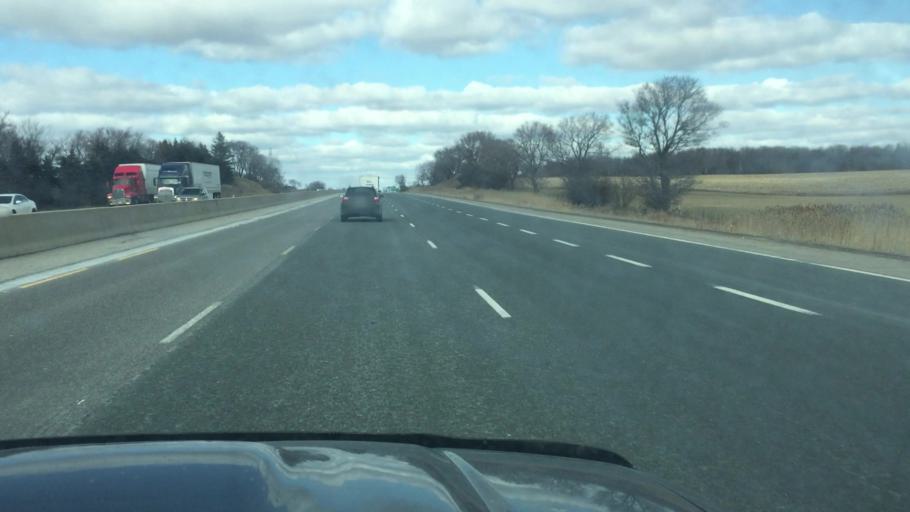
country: CA
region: Ontario
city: Ingersoll
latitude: 43.0307
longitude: -80.8494
